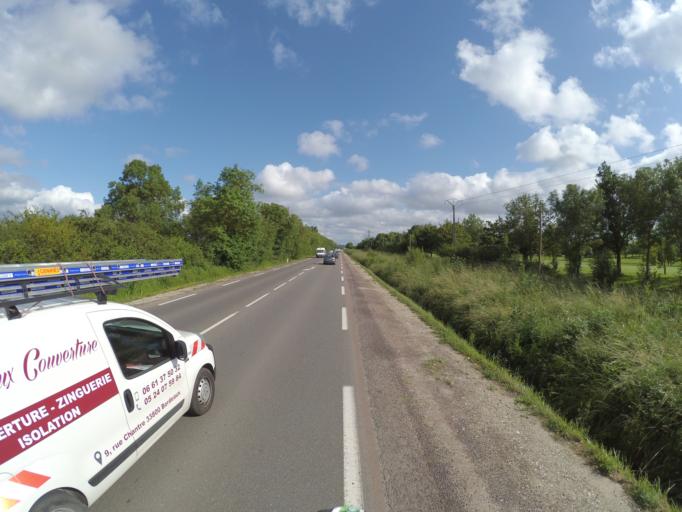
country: FR
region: Aquitaine
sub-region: Departement de la Gironde
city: Bassens
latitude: 44.9099
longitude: -0.5576
